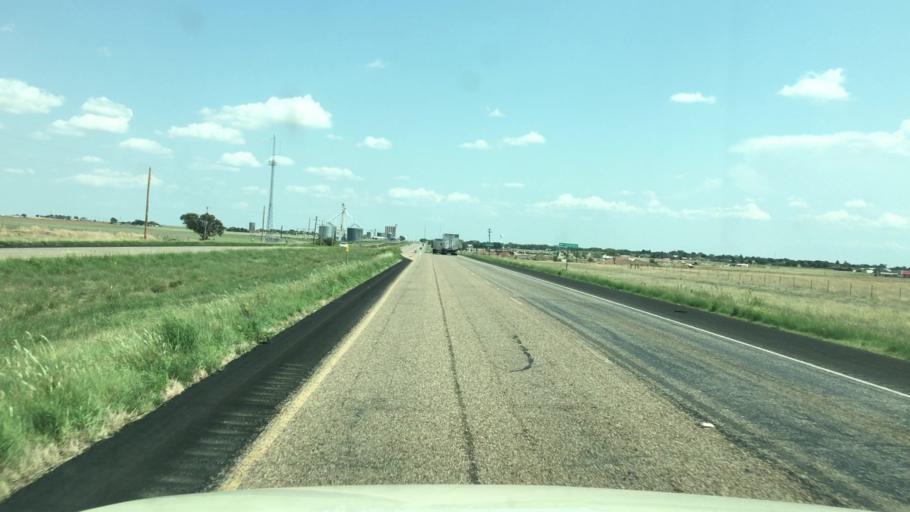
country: US
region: Texas
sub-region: Armstrong County
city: Claude
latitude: 35.1213
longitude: -101.3864
